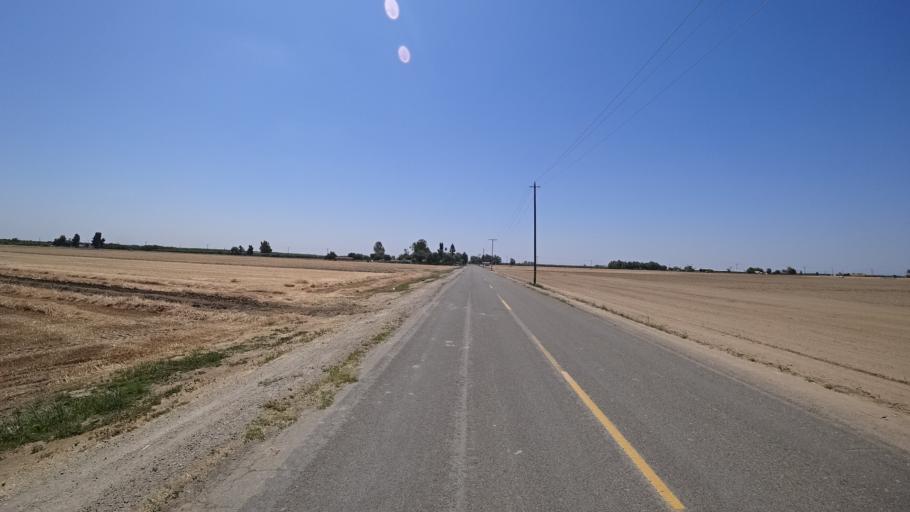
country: US
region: California
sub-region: Kings County
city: Armona
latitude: 36.3015
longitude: -119.6912
